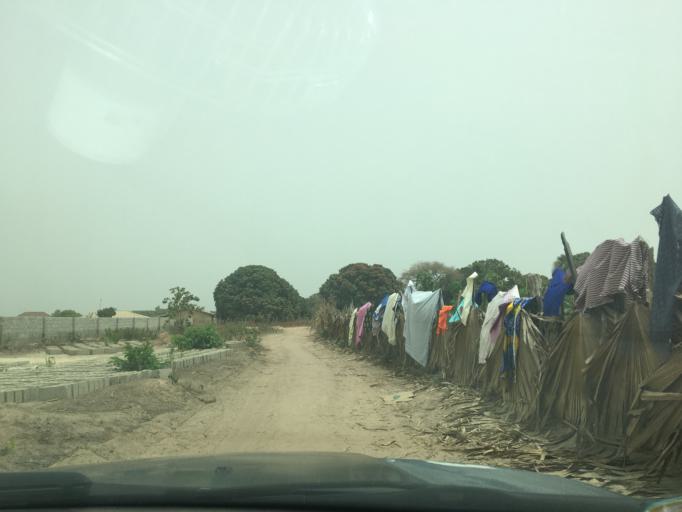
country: GM
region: Western
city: Sukuta
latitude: 13.3126
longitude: -16.7726
